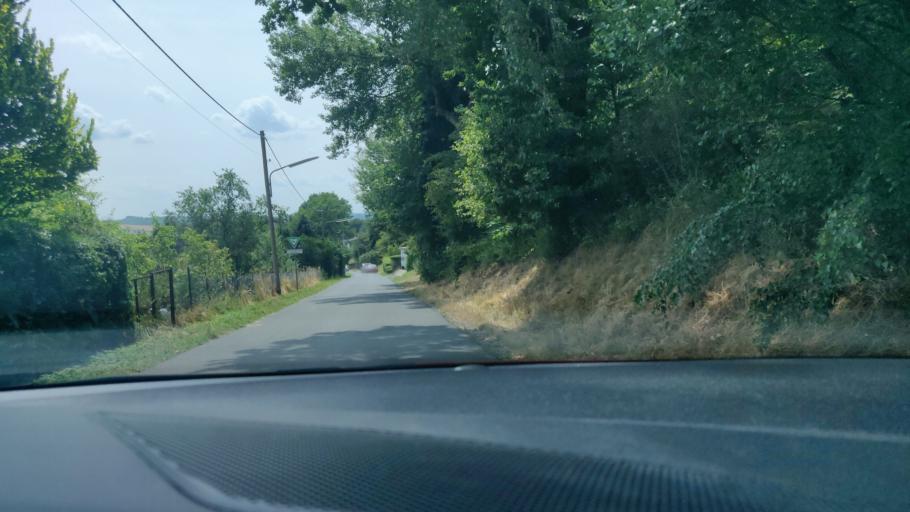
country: DE
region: North Rhine-Westphalia
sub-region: Regierungsbezirk Dusseldorf
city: Velbert
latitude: 51.3081
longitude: 7.0506
